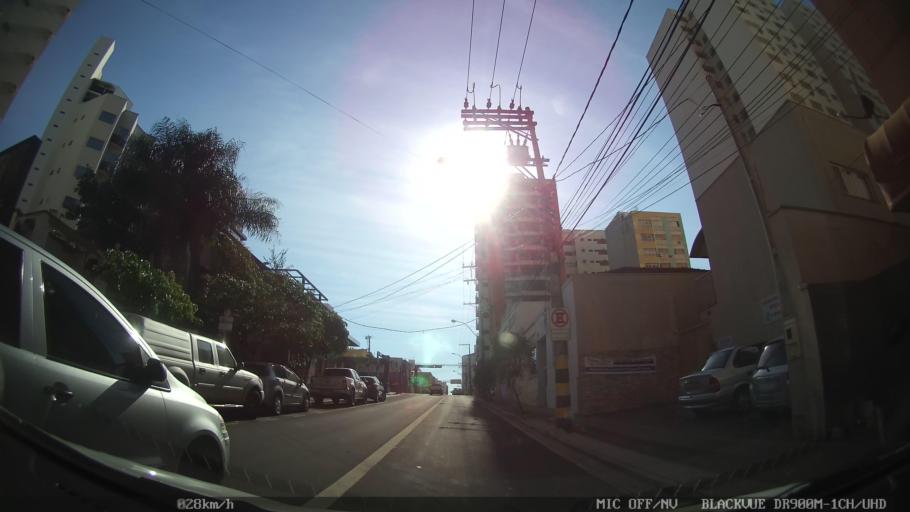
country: BR
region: Sao Paulo
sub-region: Sao Jose Do Rio Preto
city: Sao Jose do Rio Preto
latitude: -20.8155
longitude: -49.3833
